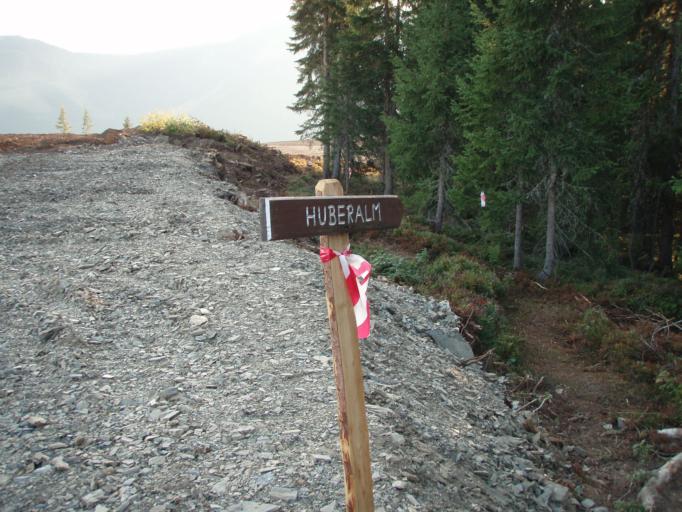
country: AT
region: Salzburg
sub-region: Politischer Bezirk Zell am See
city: Dienten am Hochkonig
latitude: 47.3538
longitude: 13.0307
